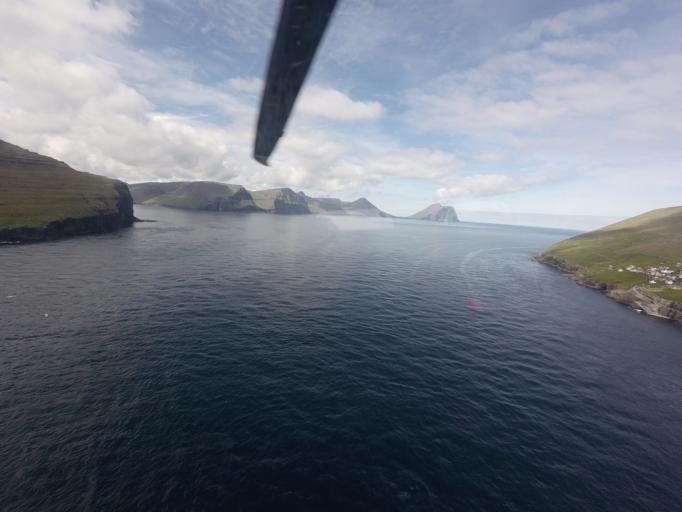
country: FO
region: Nordoyar
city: Klaksvik
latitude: 62.3113
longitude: -6.3074
